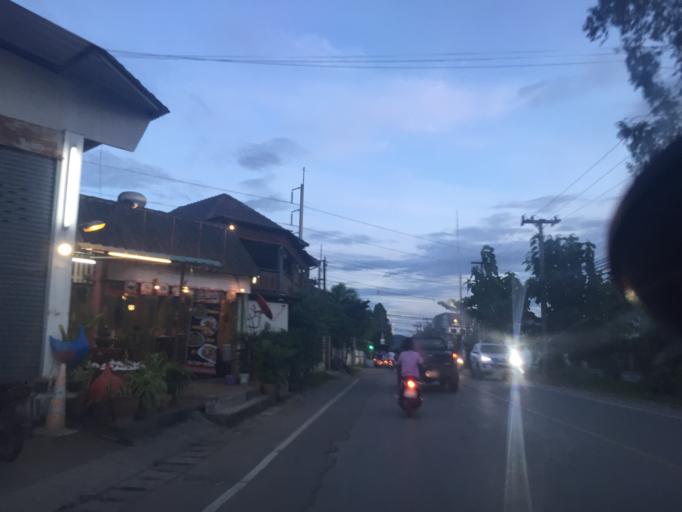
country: TH
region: Lamphun
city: Lamphun
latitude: 18.5506
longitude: 99.0356
